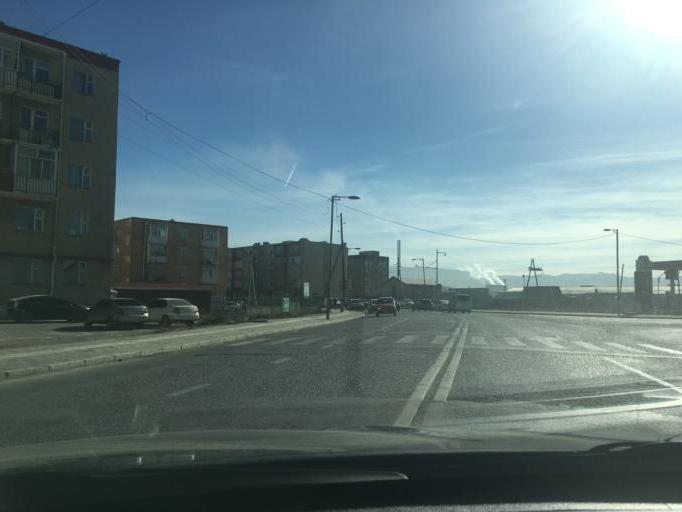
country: MN
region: Ulaanbaatar
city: Ulaanbaatar
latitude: 47.9113
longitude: 106.7840
